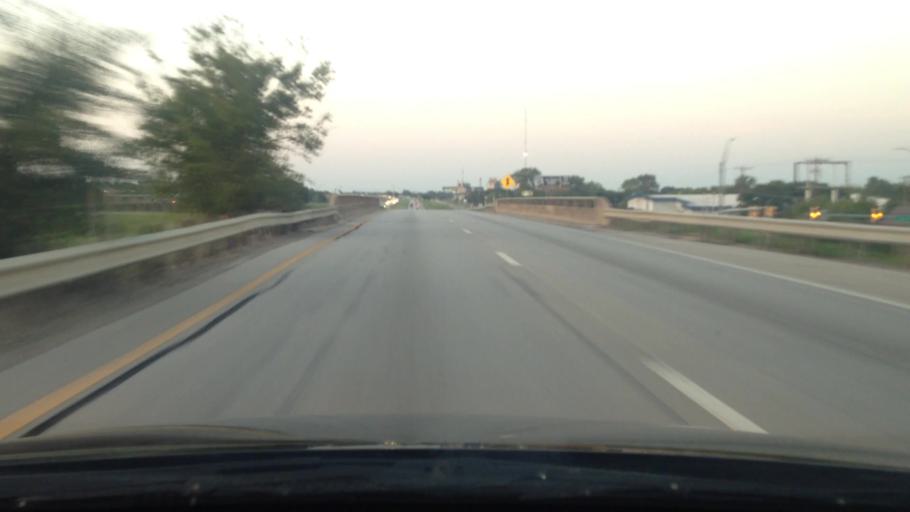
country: US
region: Texas
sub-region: Tarrant County
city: Forest Hill
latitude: 32.7076
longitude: -97.2316
